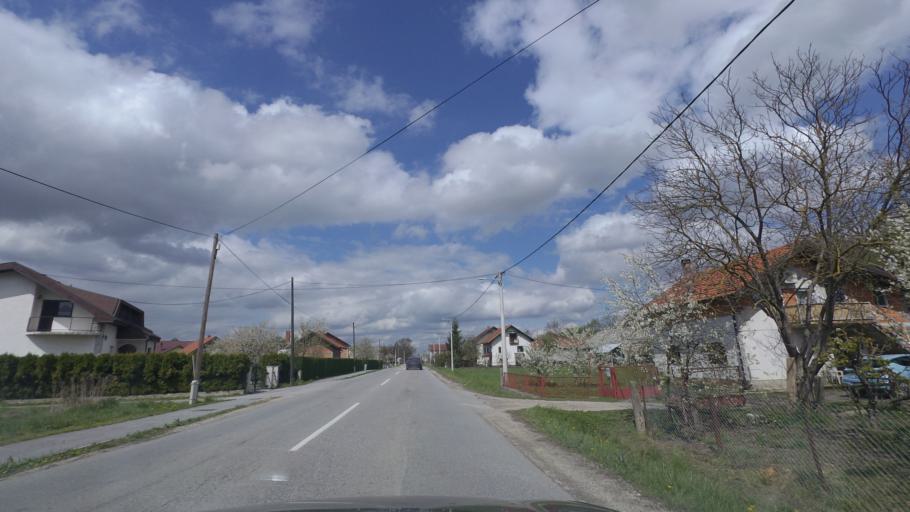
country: HR
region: Zagrebacka
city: Kerestinec
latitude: 45.7535
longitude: 15.8092
